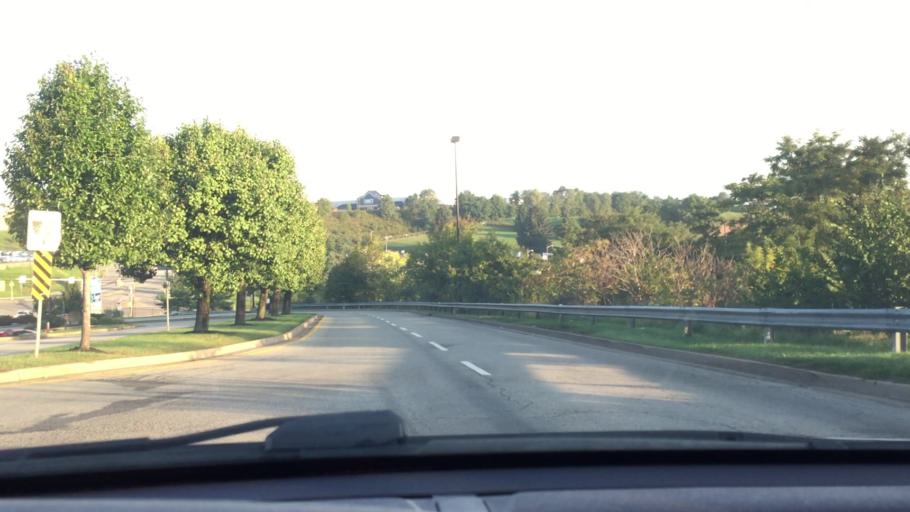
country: US
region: Pennsylvania
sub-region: Washington County
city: East Washington
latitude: 40.1851
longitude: -80.2213
